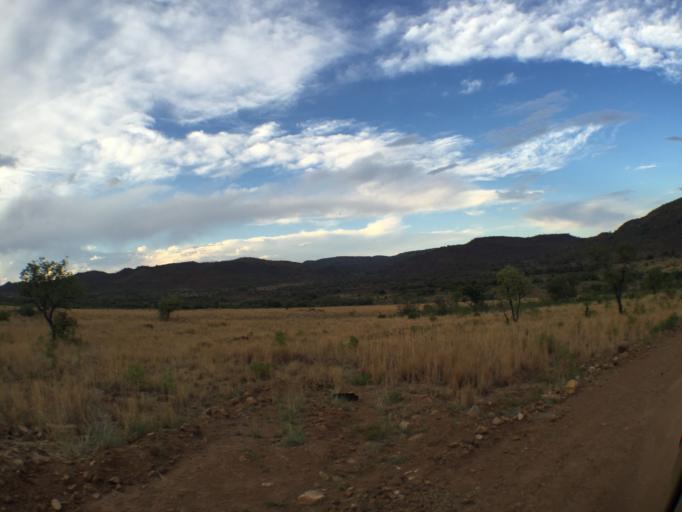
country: ZA
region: North-West
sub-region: Bojanala Platinum District Municipality
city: Mogwase
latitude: -25.2266
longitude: 27.0772
